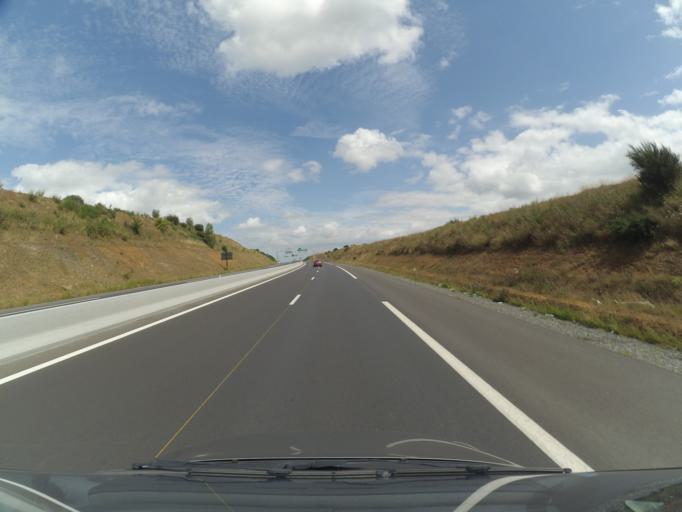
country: FR
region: Brittany
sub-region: Departement des Cotes-d'Armor
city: Langueux
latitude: 48.4776
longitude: -2.7065
